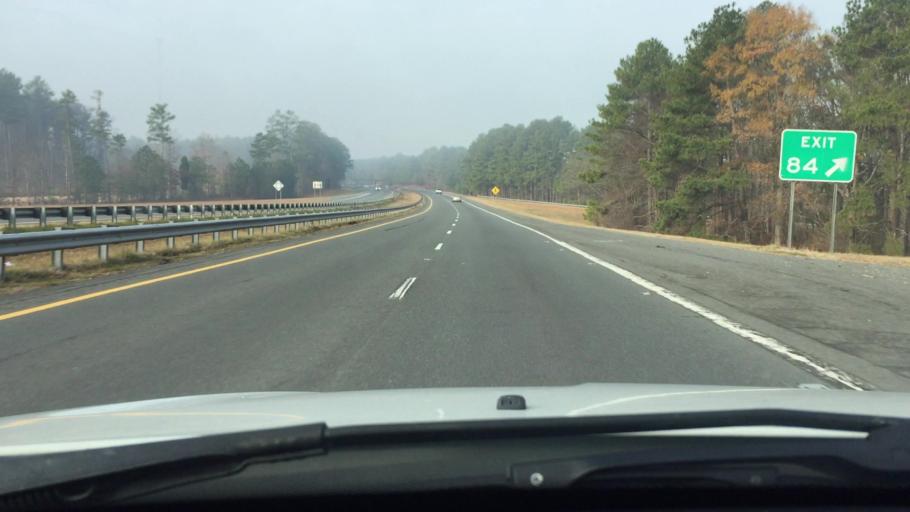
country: US
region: North Carolina
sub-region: Wake County
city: Green Level
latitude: 35.6445
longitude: -79.0049
